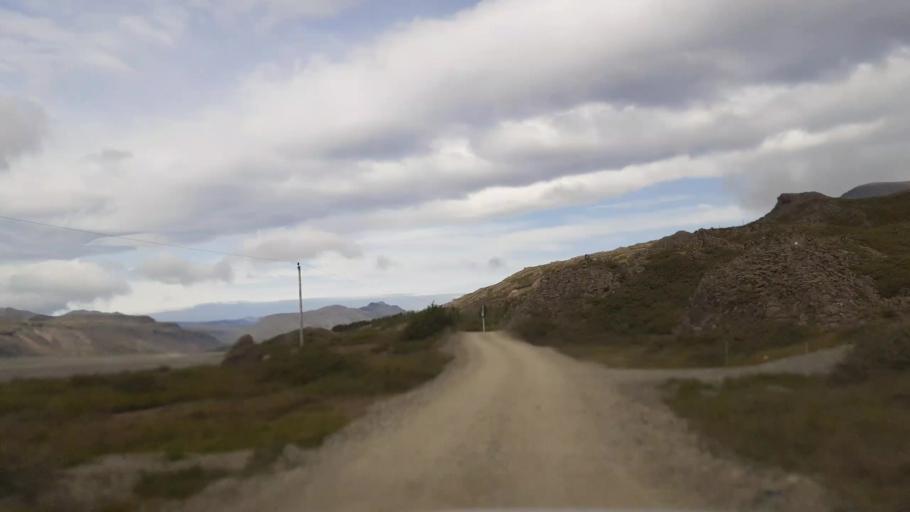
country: IS
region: East
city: Hoefn
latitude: 64.4334
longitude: -14.8935
